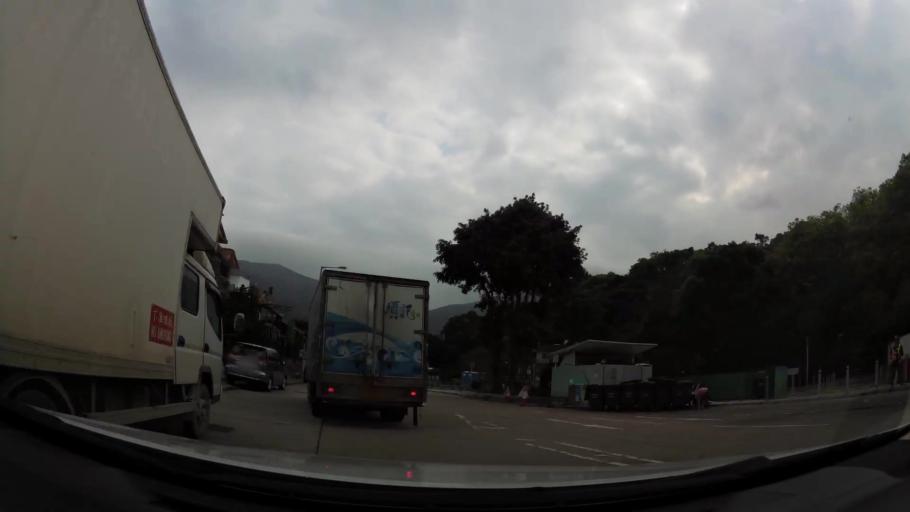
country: HK
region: Tai Po
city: Tai Po
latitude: 22.4381
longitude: 114.1648
